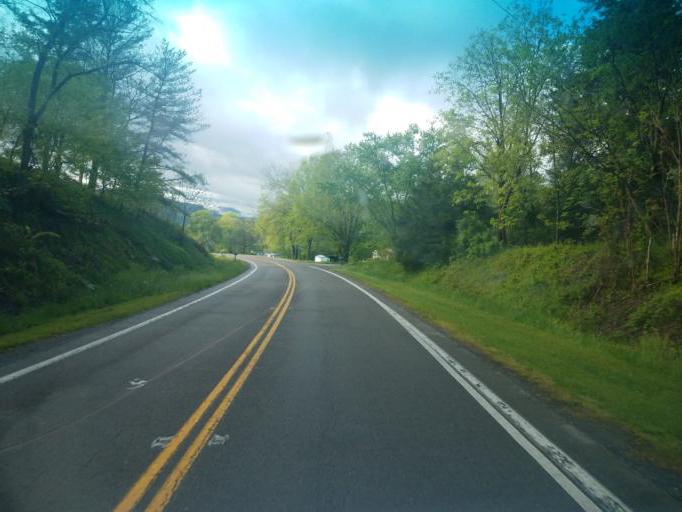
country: US
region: Virginia
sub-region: Washington County
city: Emory
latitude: 36.6808
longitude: -81.8146
